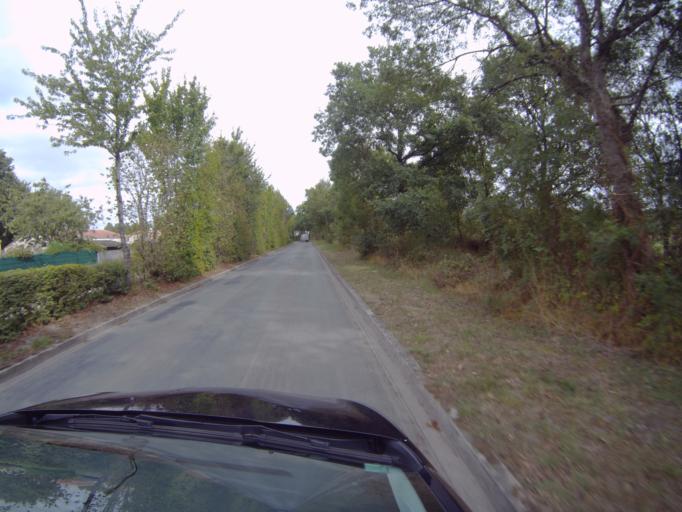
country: FR
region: Pays de la Loire
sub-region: Departement de la Vendee
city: Saint-Hilaire-de-Loulay
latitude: 46.9958
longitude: -1.3329
